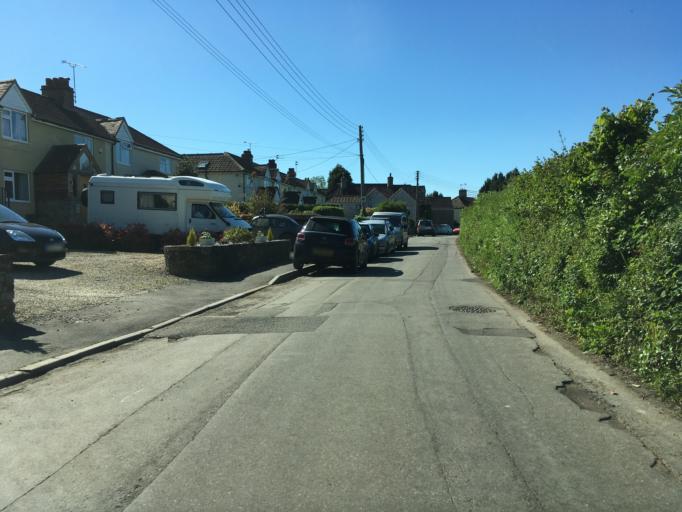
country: GB
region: England
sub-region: South Gloucestershire
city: Almondsbury
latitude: 51.5863
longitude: -2.5766
